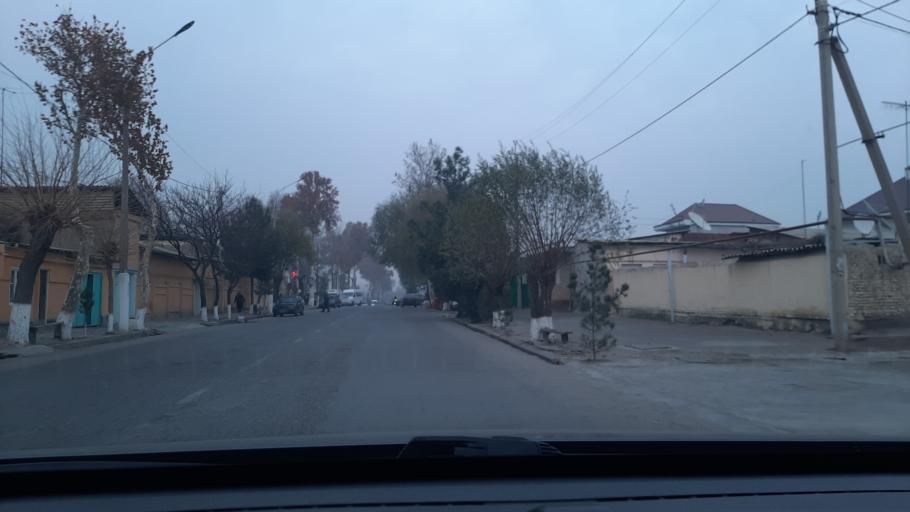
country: TJ
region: Viloyati Sughd
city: Khujand
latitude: 40.2630
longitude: 69.5992
